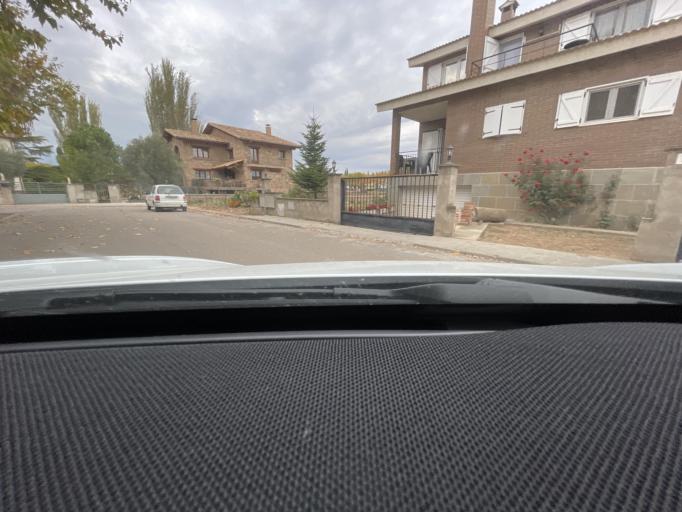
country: ES
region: Catalonia
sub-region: Provincia de Lleida
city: Solsona
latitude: 41.9967
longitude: 1.5270
